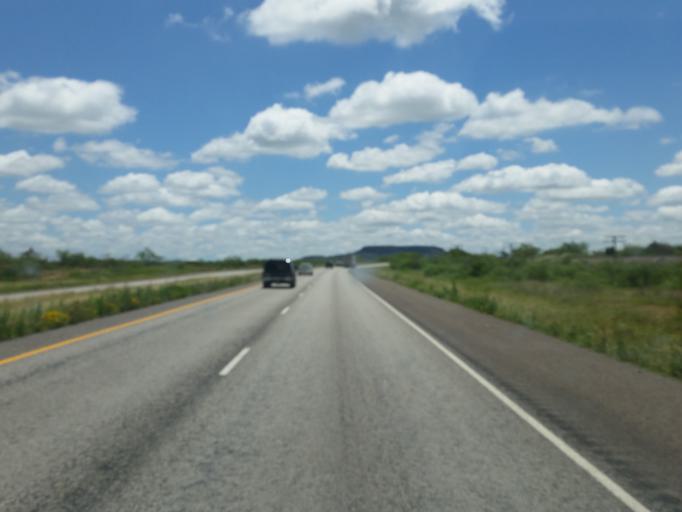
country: US
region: Texas
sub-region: Scurry County
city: Snyder
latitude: 32.9804
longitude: -101.1095
